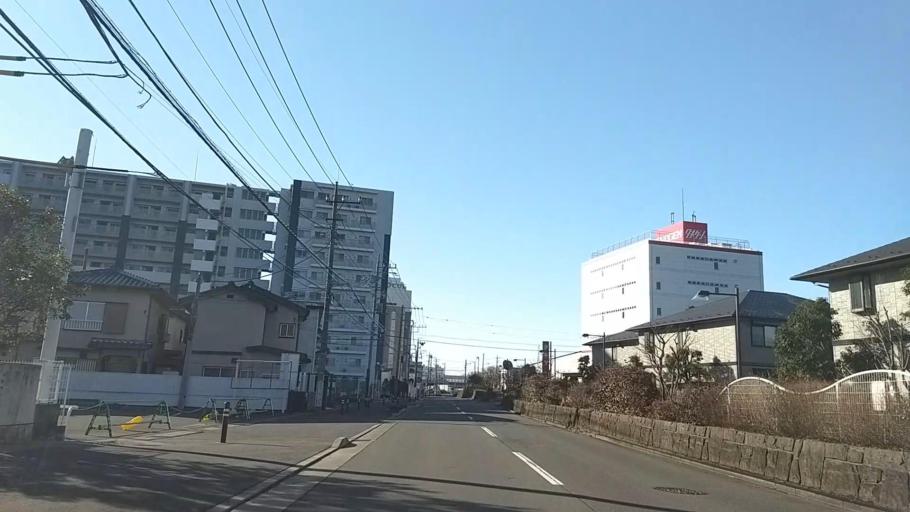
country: JP
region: Kanagawa
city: Atsugi
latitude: 35.4285
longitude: 139.3587
